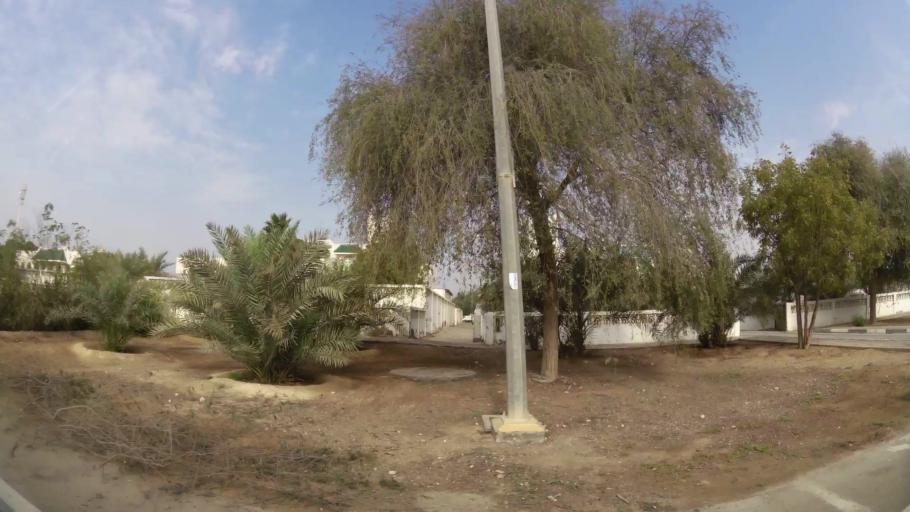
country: AE
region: Abu Dhabi
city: Abu Dhabi
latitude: 24.6672
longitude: 54.7664
